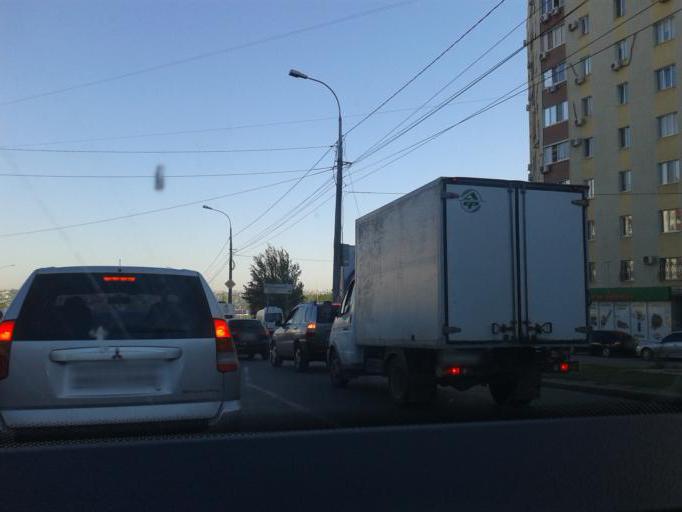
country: RU
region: Volgograd
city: Volgograd
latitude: 48.6784
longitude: 44.4452
